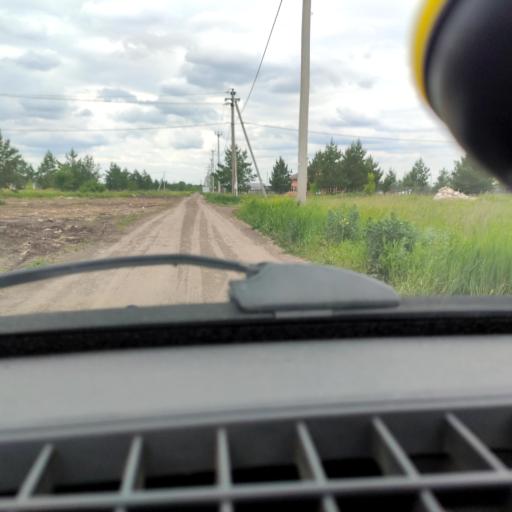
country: RU
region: Samara
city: Povolzhskiy
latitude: 53.5961
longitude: 49.5807
